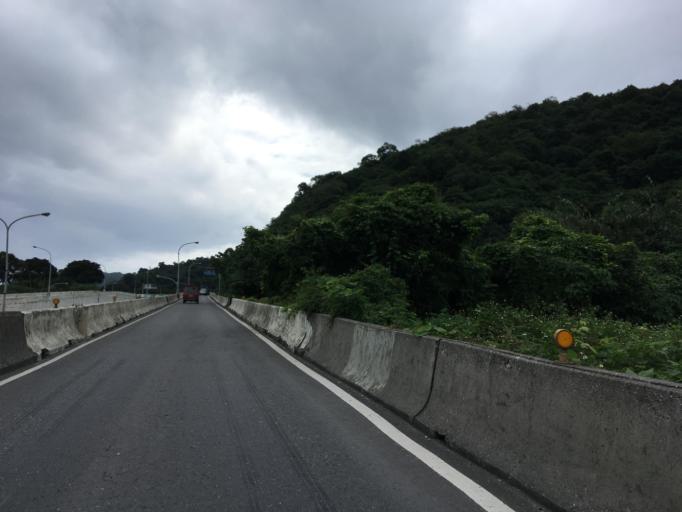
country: TW
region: Taiwan
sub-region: Yilan
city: Yilan
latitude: 24.6148
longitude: 121.8225
